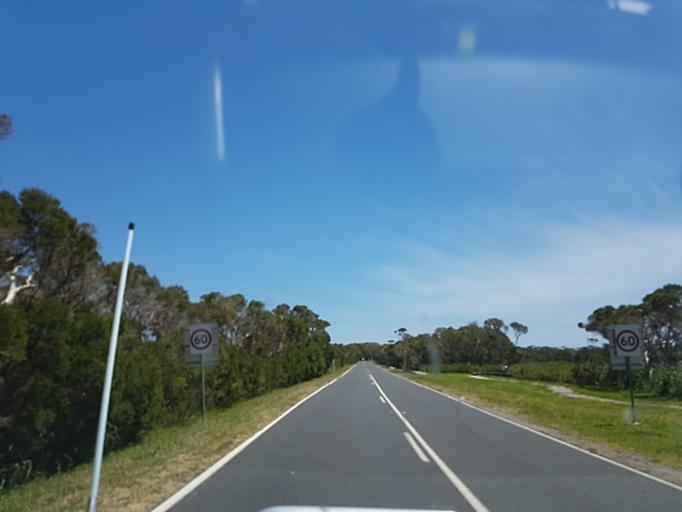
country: AU
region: Victoria
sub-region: Bass Coast
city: North Wonthaggi
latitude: -38.7006
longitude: 145.8763
